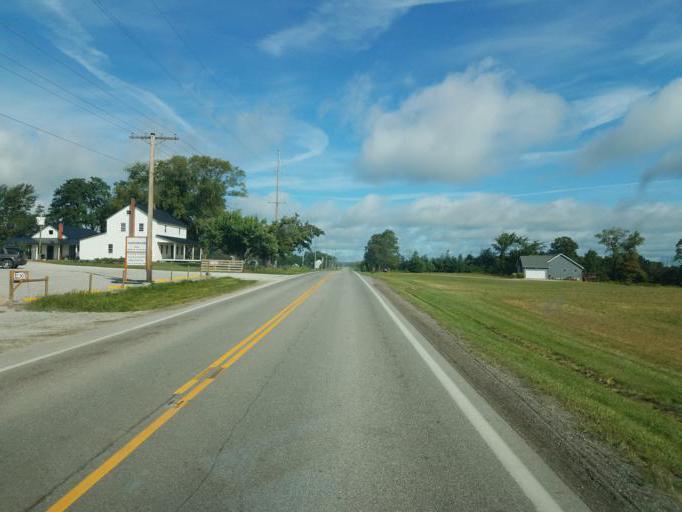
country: US
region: Ohio
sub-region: Wayne County
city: West Salem
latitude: 40.9962
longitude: -82.1119
